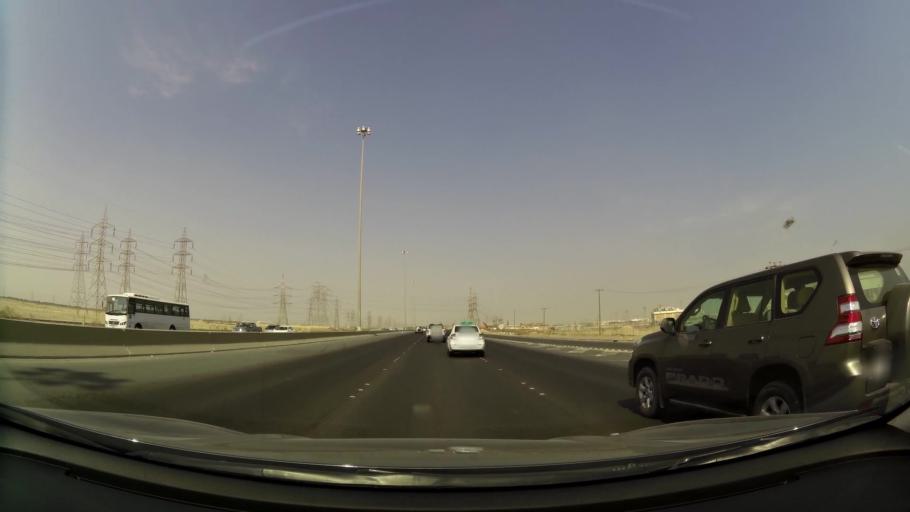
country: KW
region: Al Ahmadi
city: Al Fahahil
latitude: 29.0512
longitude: 48.1118
